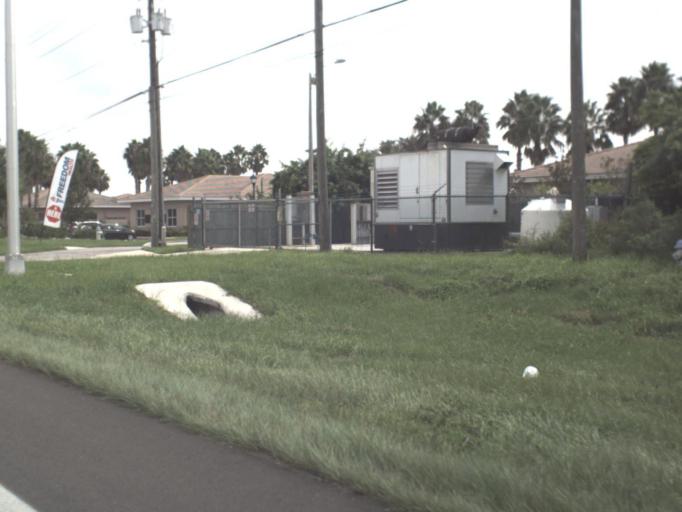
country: US
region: Florida
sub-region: Manatee County
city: Ellenton
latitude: 27.4984
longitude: -82.5145
